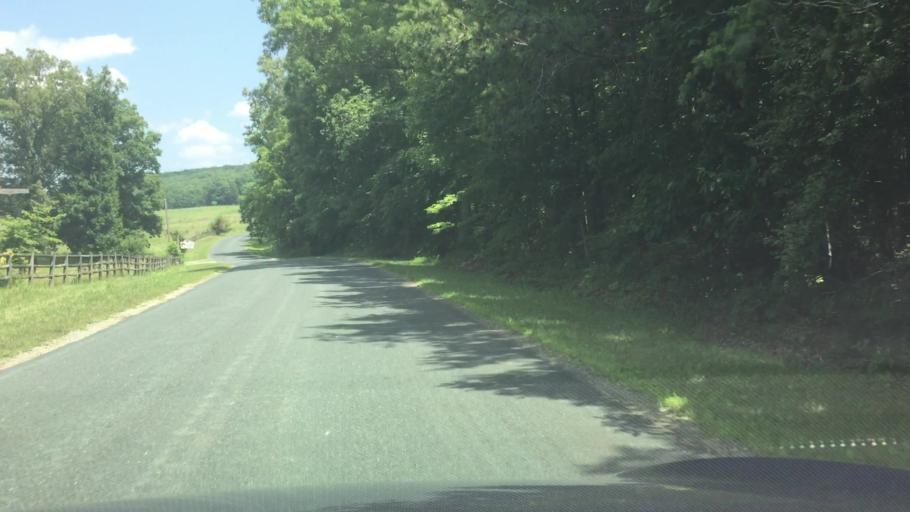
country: US
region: Virginia
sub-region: Appomattox County
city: Appomattox
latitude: 37.3222
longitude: -78.8584
